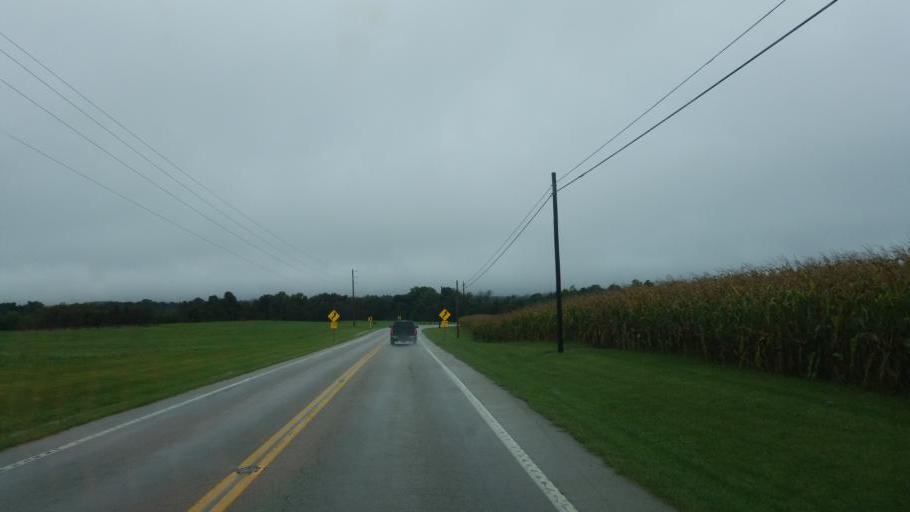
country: US
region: Ohio
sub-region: Adams County
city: West Union
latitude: 38.7978
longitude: -83.5005
